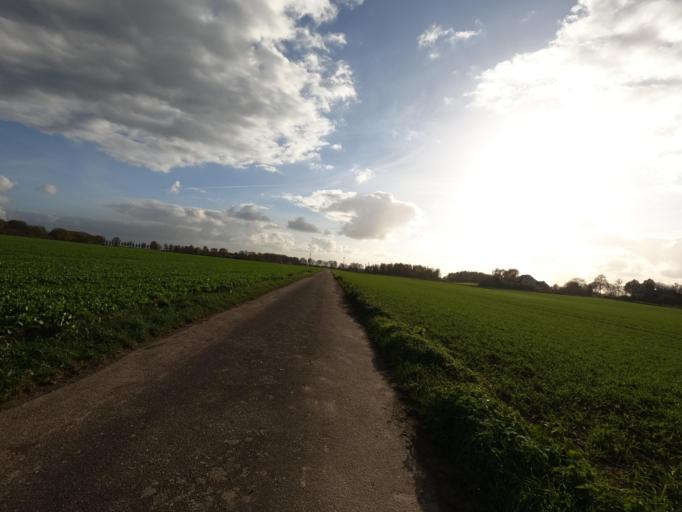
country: DE
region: North Rhine-Westphalia
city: Geilenkirchen
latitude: 50.9570
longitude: 6.1323
